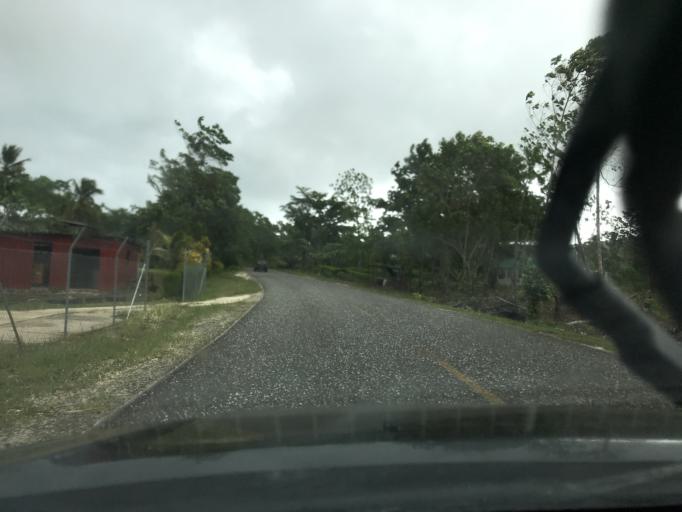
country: SB
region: Western Province
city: Gizo
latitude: -8.3196
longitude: 157.2559
